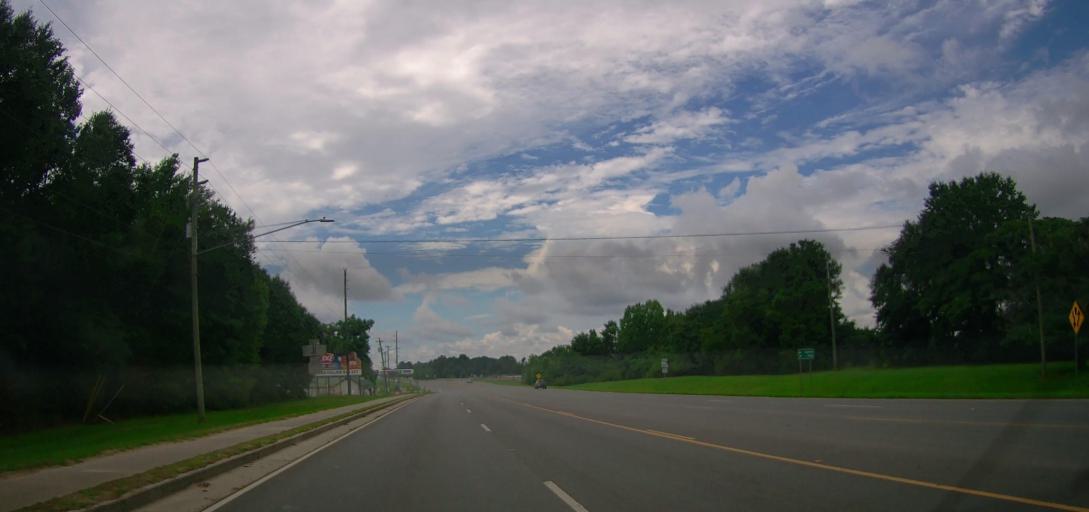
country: US
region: Georgia
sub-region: Dodge County
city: Eastman
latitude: 32.1059
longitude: -83.0724
